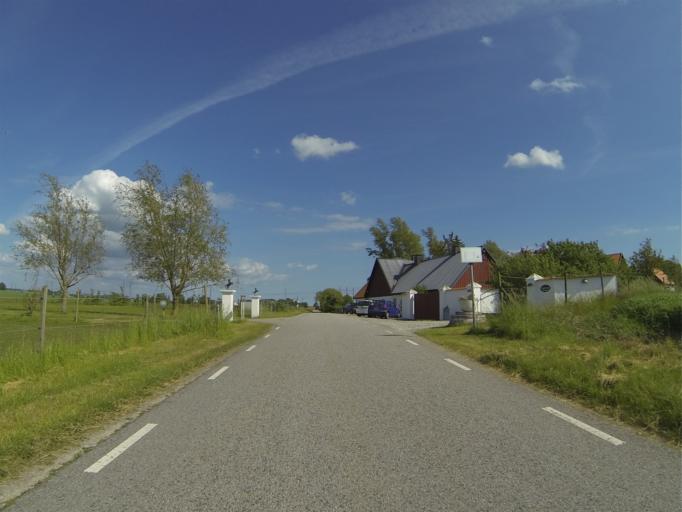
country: SE
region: Skane
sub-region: Staffanstorps Kommun
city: Hjaerup
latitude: 55.6335
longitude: 13.1280
